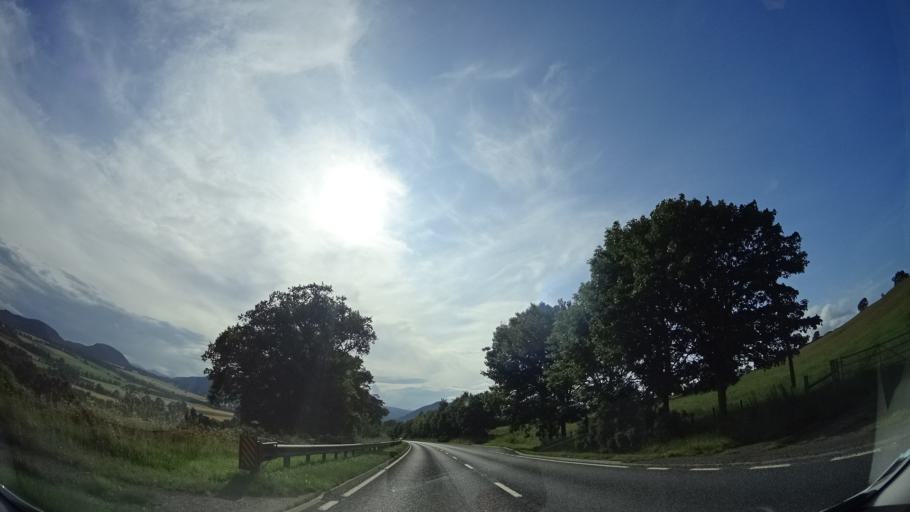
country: GB
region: Scotland
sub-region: Highland
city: Muir of Ord
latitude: 57.5585
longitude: -4.5283
